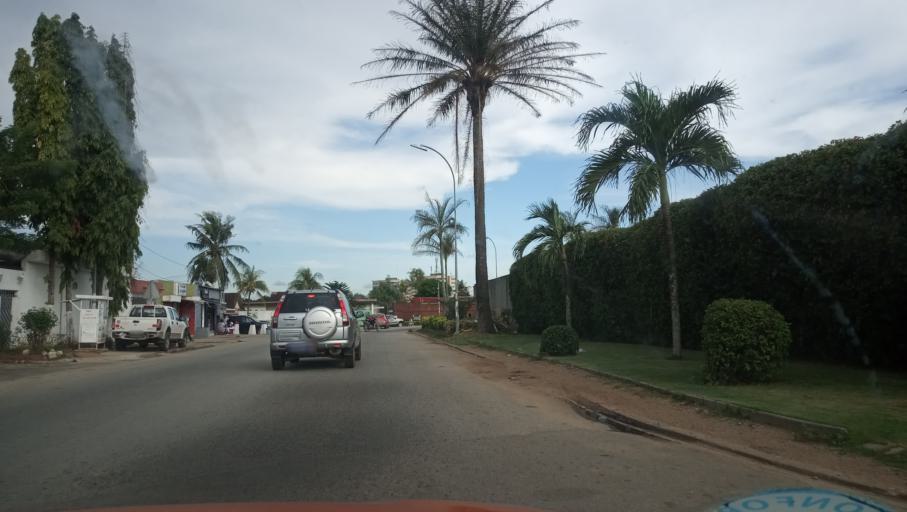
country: CI
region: Lagunes
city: Abidjan
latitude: 5.3485
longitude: -3.9804
